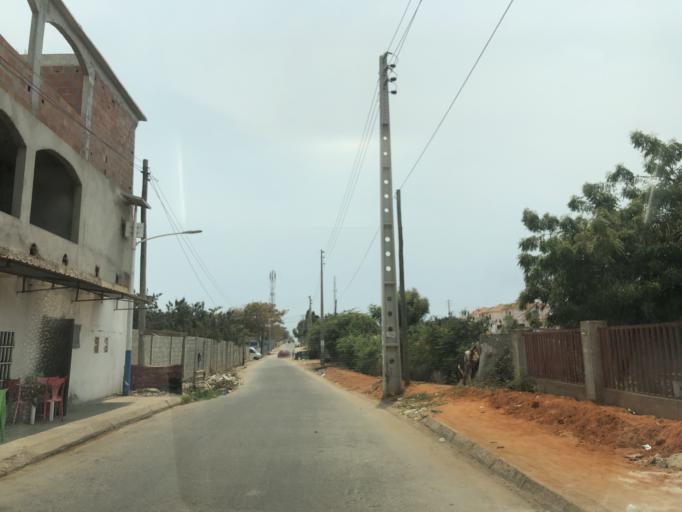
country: AO
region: Luanda
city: Luanda
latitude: -8.8896
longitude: 13.1982
